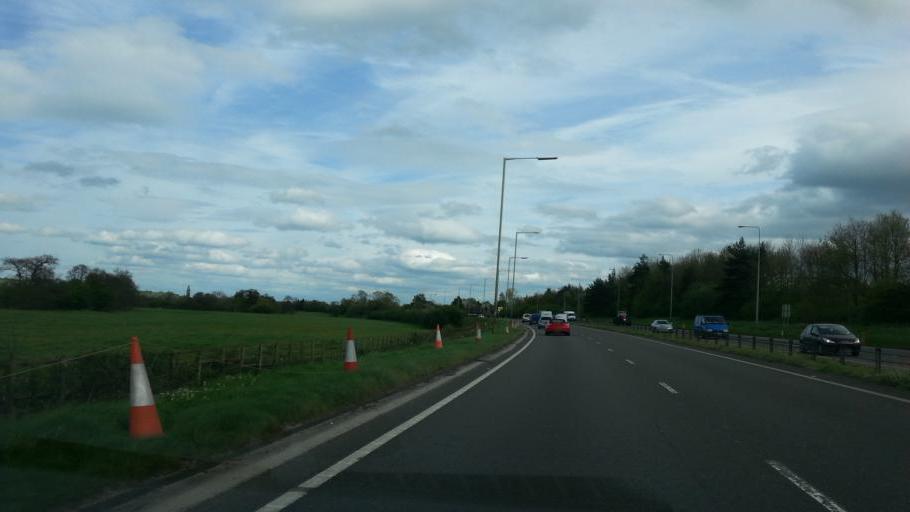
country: GB
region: England
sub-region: Staffordshire
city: Uttoxeter
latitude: 52.9101
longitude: -1.8869
